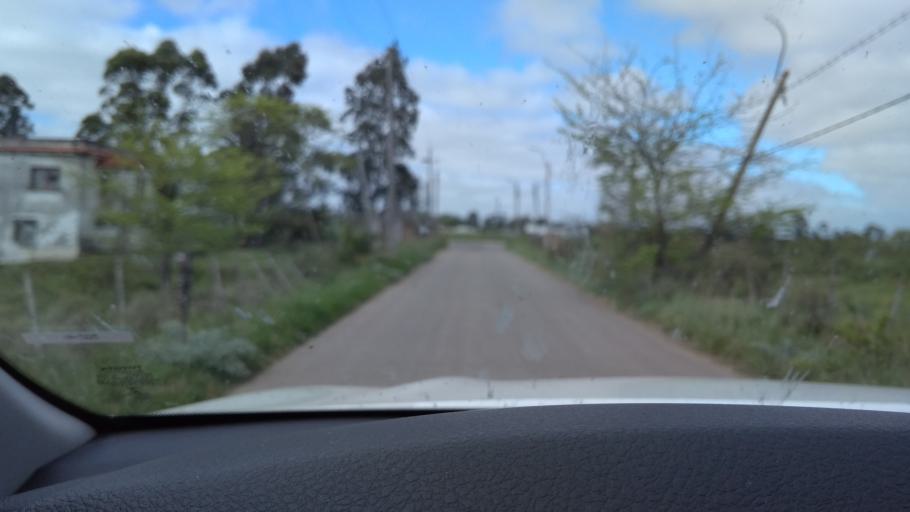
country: UY
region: Canelones
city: Toledo
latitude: -34.7741
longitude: -56.1092
